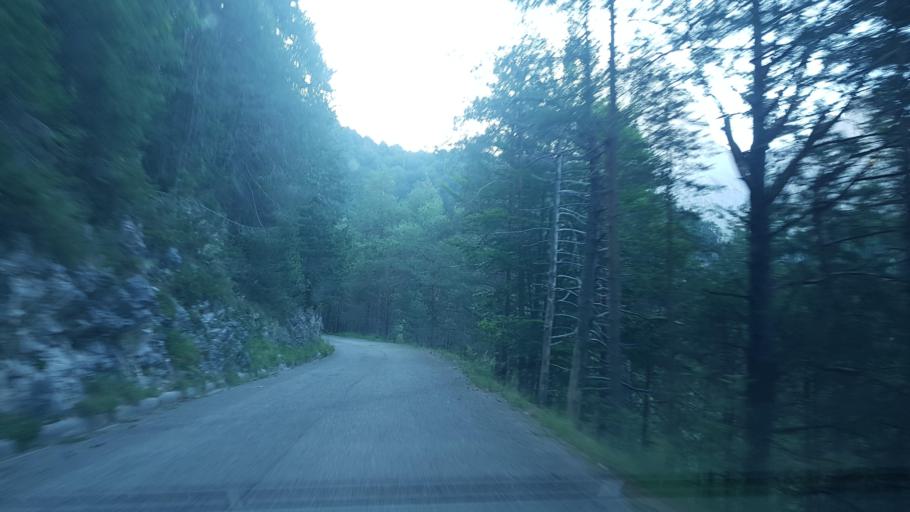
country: IT
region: Friuli Venezia Giulia
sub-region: Provincia di Udine
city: Malborghetto
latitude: 46.4595
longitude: 13.3864
